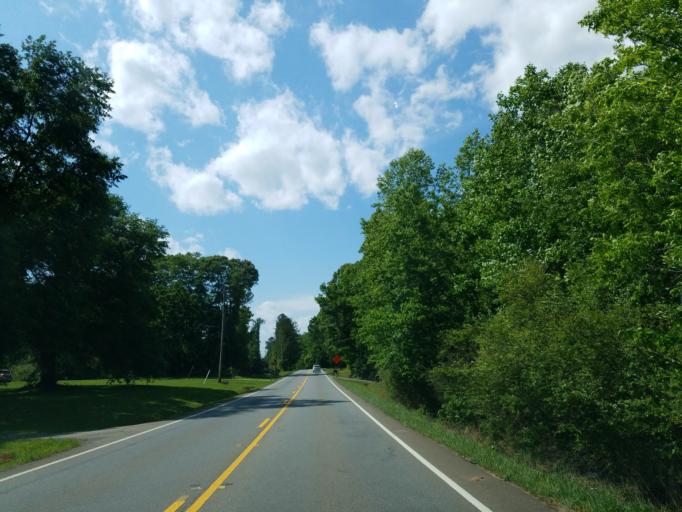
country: US
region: Georgia
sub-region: Cherokee County
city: Ball Ground
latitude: 34.2684
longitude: -84.2916
